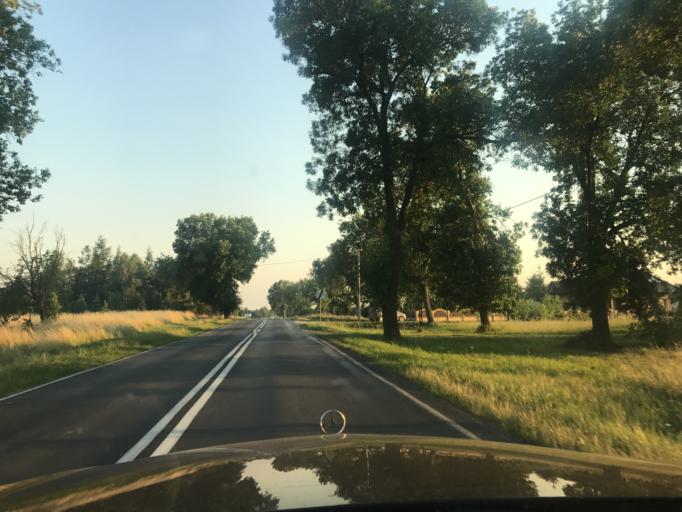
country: PL
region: Lublin Voivodeship
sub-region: Powiat lubartowski
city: Lubartow
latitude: 51.4950
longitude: 22.6359
